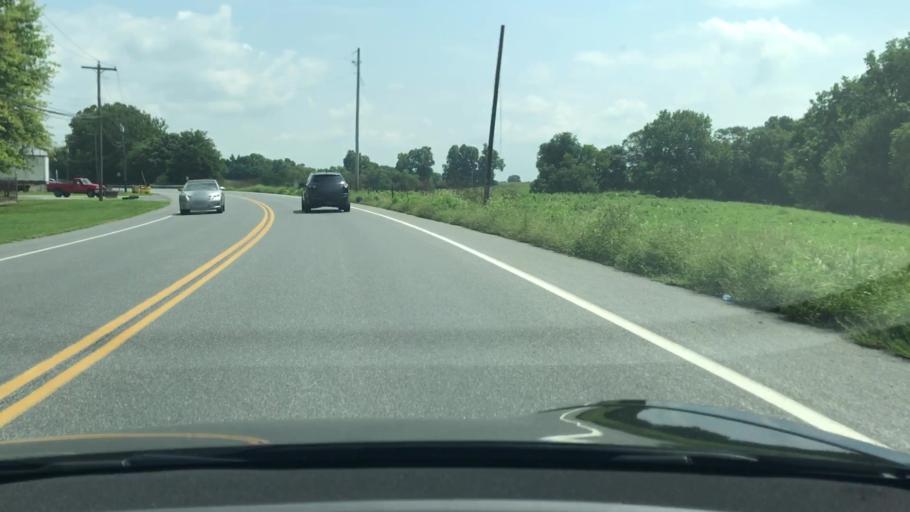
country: US
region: Pennsylvania
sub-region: Lancaster County
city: Salunga
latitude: 40.1058
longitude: -76.4466
